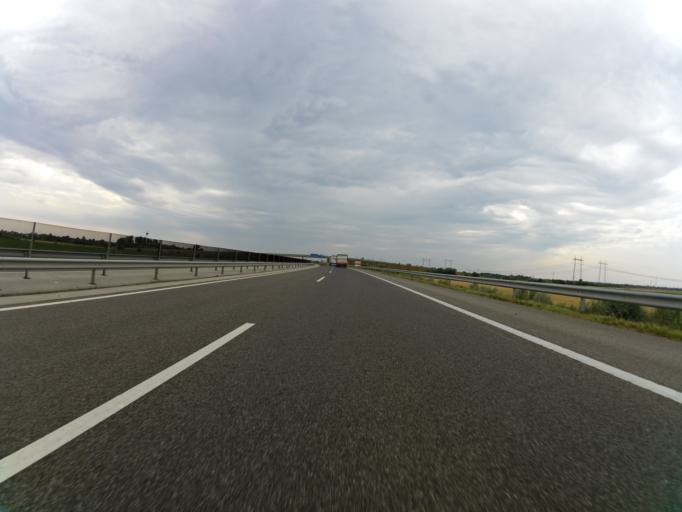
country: HU
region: Csongrad
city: Sandorfalva
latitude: 46.2961
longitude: 20.0948
